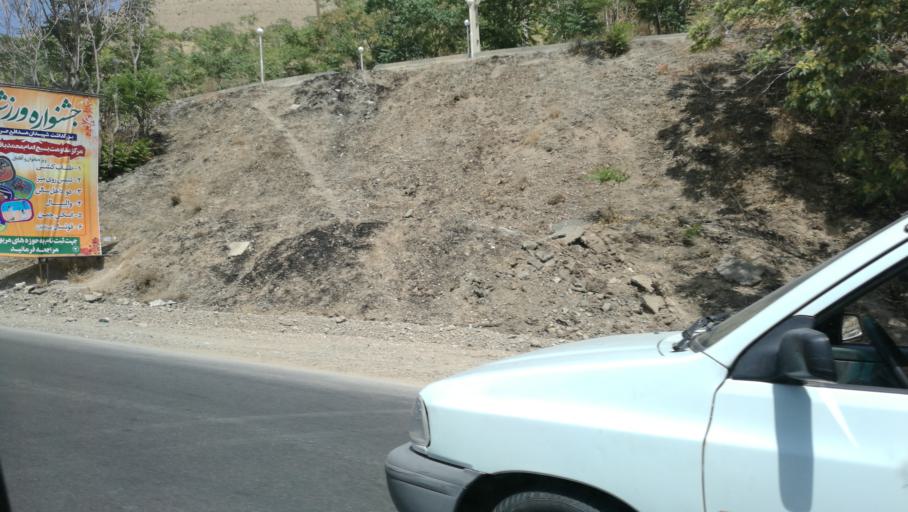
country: IR
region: Alborz
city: Karaj
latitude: 35.9288
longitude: 51.0609
